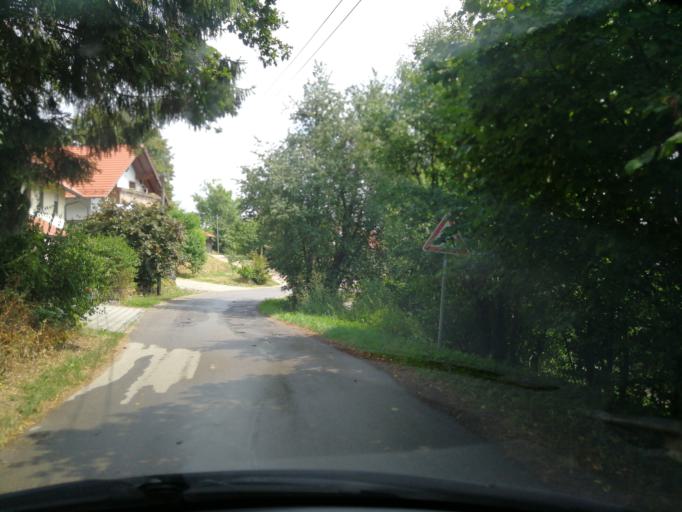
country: DE
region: Bavaria
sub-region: Upper Palatinate
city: Brennberg
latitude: 49.0706
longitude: 12.4015
